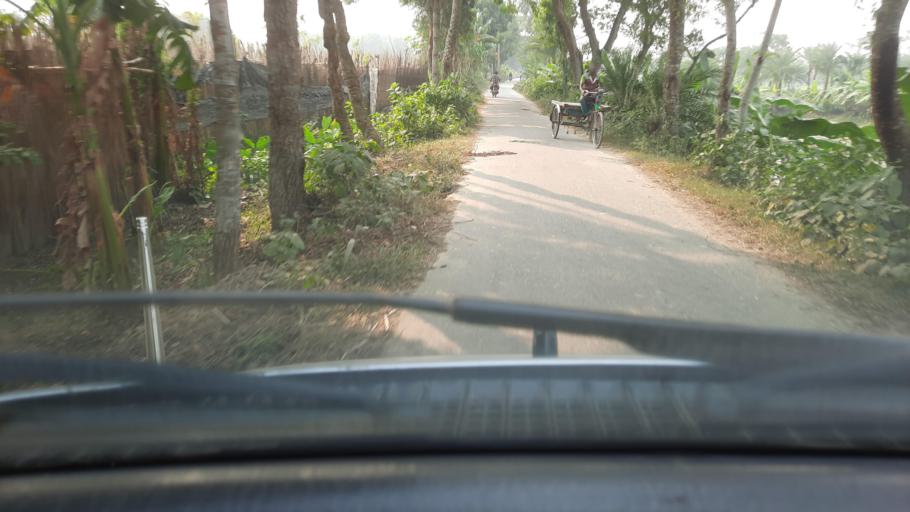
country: BD
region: Khulna
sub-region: Chuadanga
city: Nowlamary
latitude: 23.6000
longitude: 88.8480
